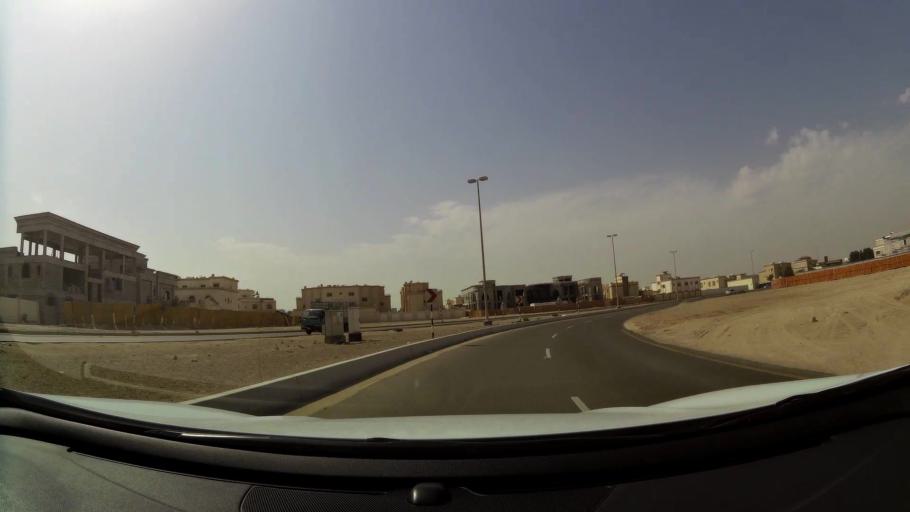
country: AE
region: Abu Dhabi
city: Abu Dhabi
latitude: 24.3321
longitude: 54.5500
